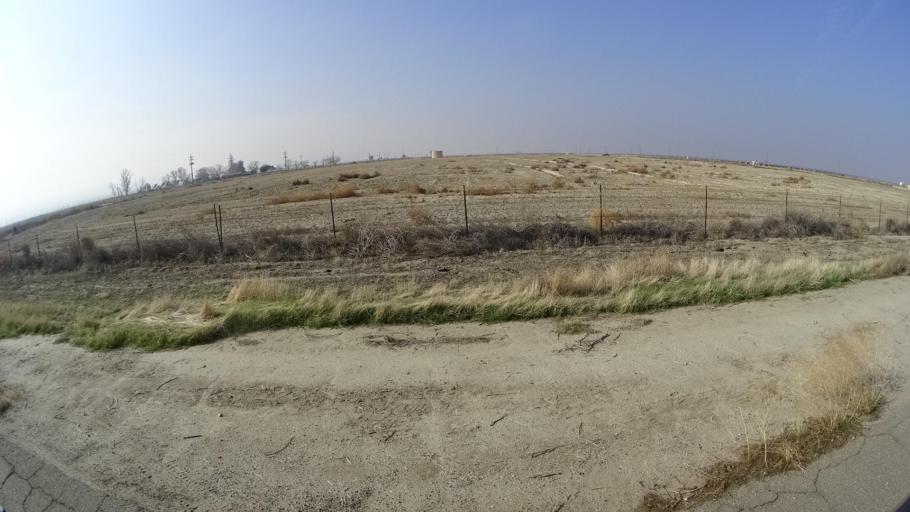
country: US
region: California
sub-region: Kern County
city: Buttonwillow
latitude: 35.3341
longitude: -119.3590
